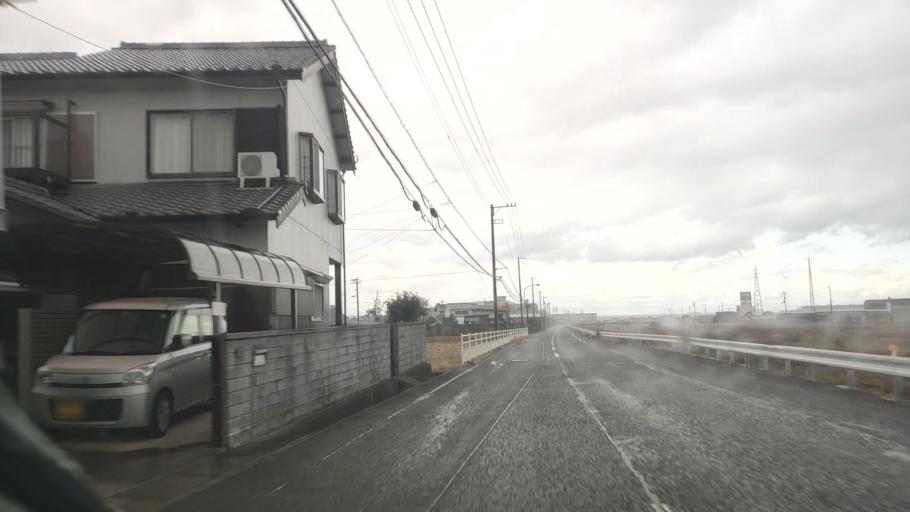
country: JP
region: Tokushima
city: Ishii
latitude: 34.2087
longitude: 134.4041
